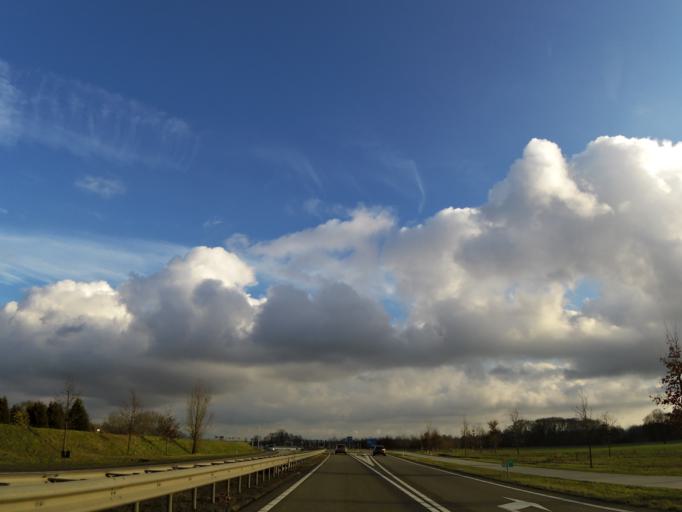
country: NL
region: Limburg
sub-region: Gemeente Sittard-Geleen
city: Limbricht
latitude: 51.0305
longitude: 5.8477
